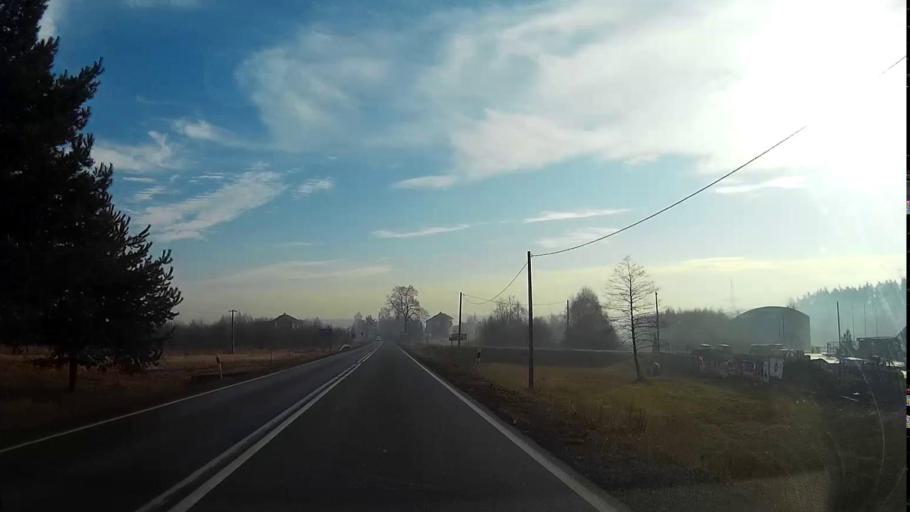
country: PL
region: Lesser Poland Voivodeship
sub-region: Powiat chrzanowski
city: Alwernia
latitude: 50.0590
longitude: 19.5194
